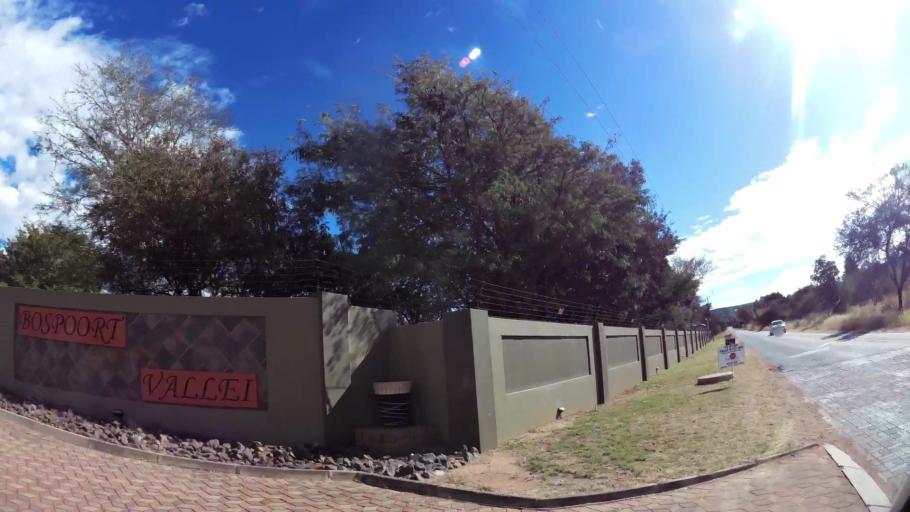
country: ZA
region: Limpopo
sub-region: Waterberg District Municipality
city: Warmbaths
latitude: -24.8683
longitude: 28.2902
